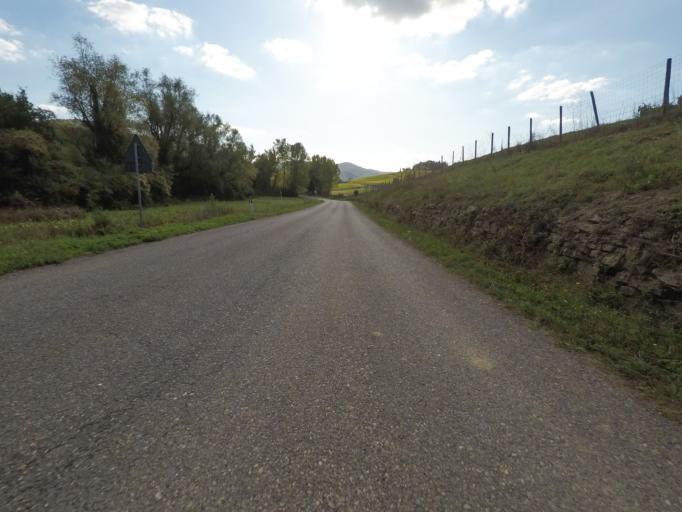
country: IT
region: Tuscany
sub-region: Provincia di Siena
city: Radda in Chianti
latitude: 43.5042
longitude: 11.3986
